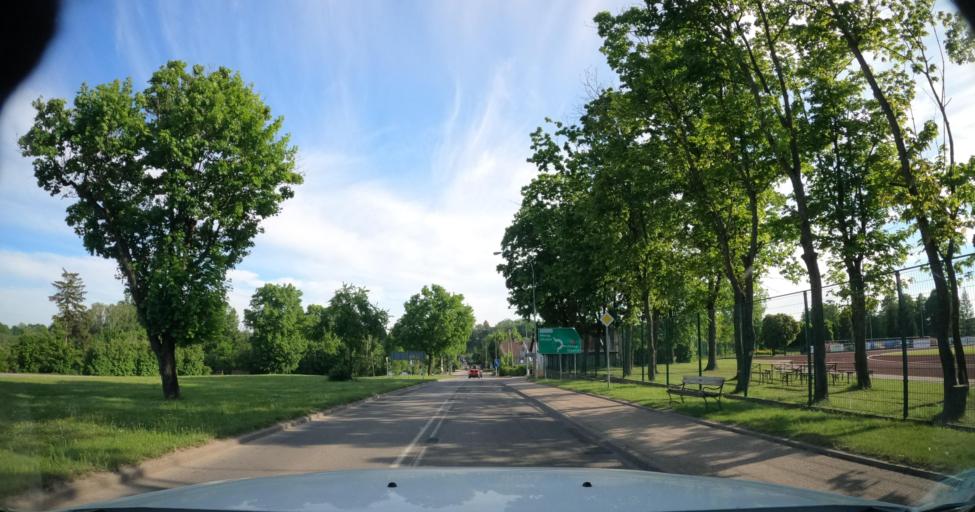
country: PL
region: Warmian-Masurian Voivodeship
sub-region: Powiat elblaski
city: Paslek
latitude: 54.0722
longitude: 19.6610
